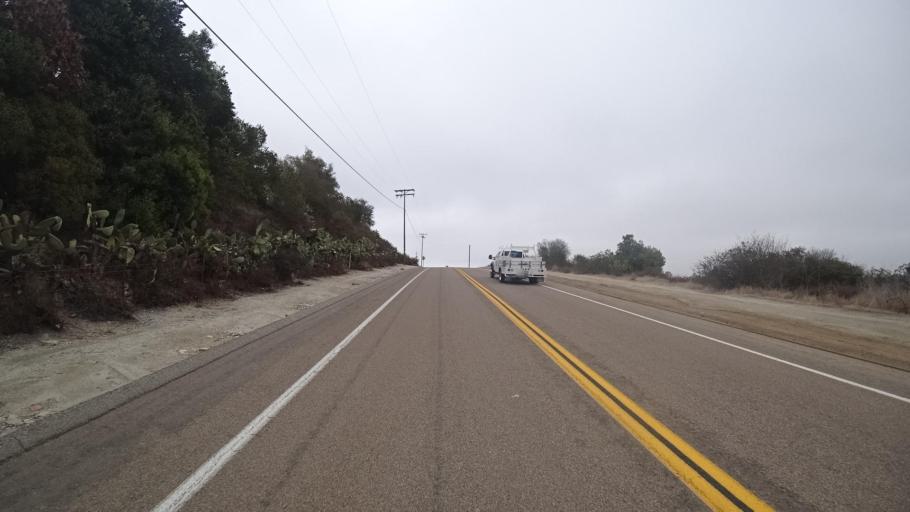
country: US
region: California
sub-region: San Diego County
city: Rainbow
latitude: 33.3862
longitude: -117.1721
